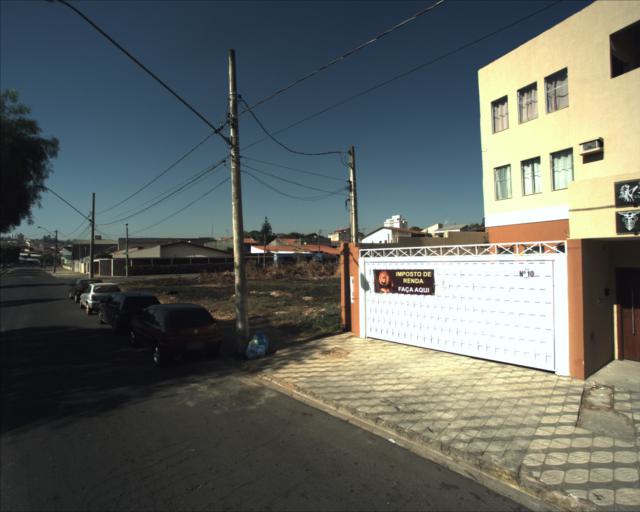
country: BR
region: Sao Paulo
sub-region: Sorocaba
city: Sorocaba
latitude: -23.5067
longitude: -47.4350
